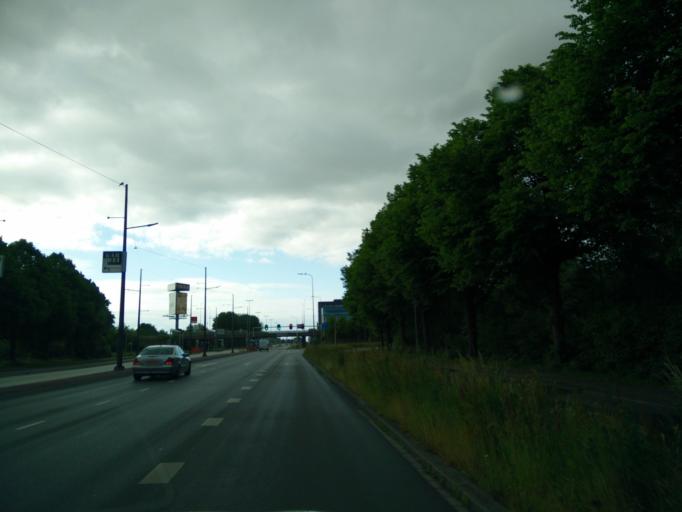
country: NL
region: Groningen
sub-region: Gemeente Groningen
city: Oosterpark
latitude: 53.2128
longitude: 6.5861
